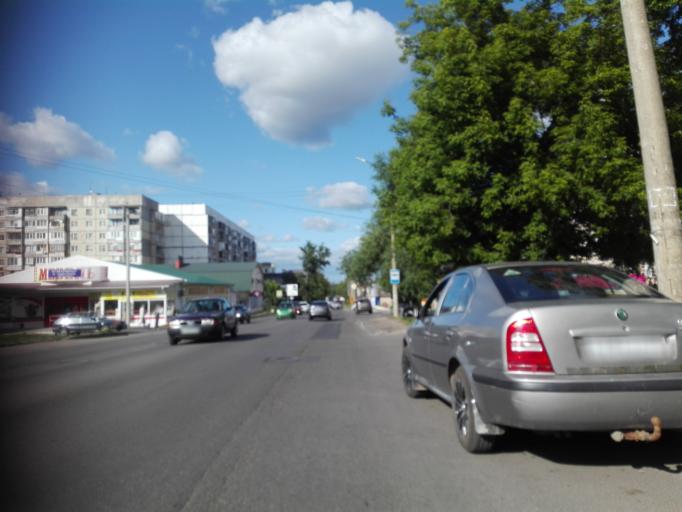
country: RU
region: Orjol
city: Orel
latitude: 52.9509
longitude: 36.0419
